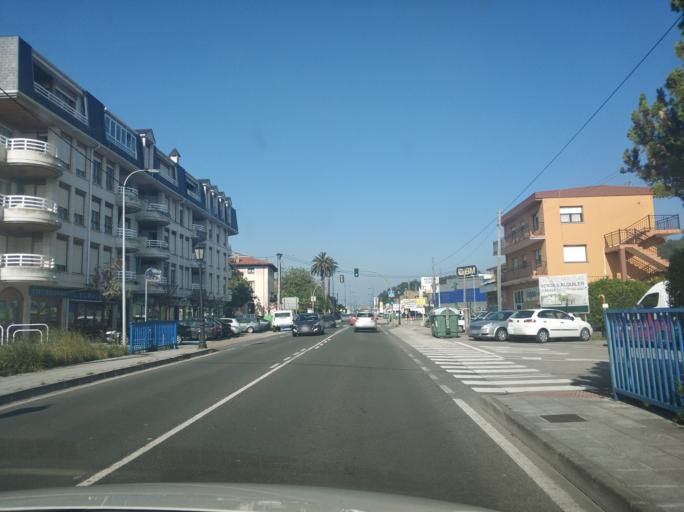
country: ES
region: Cantabria
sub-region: Provincia de Cantabria
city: Colindres
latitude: 43.3973
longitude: -3.4452
